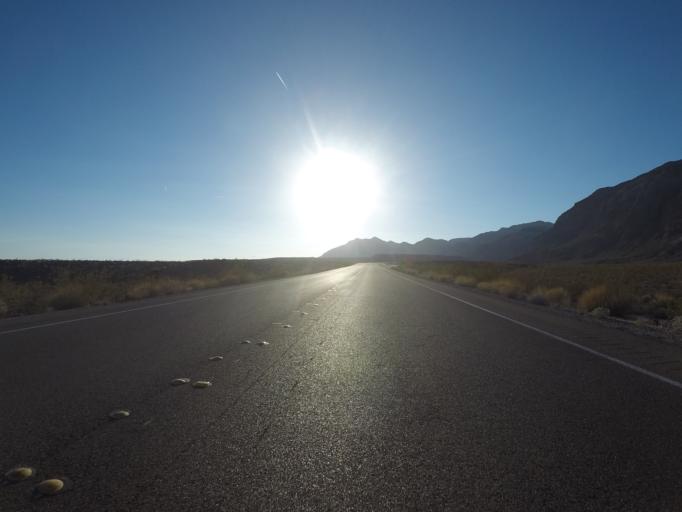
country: US
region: Nevada
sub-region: Clark County
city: Moapa Valley
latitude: 36.3669
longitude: -114.4519
